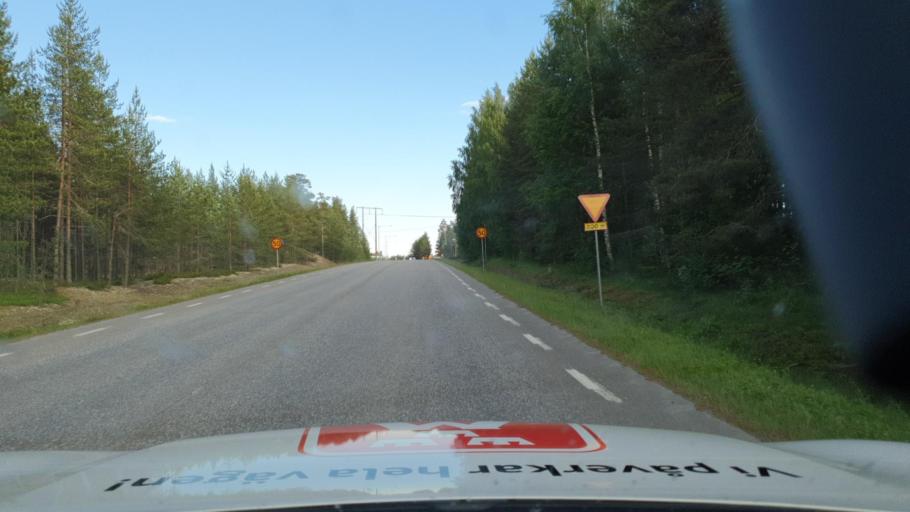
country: SE
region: Vaesterbotten
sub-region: Umea Kommun
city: Roback
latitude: 63.8501
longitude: 20.1545
